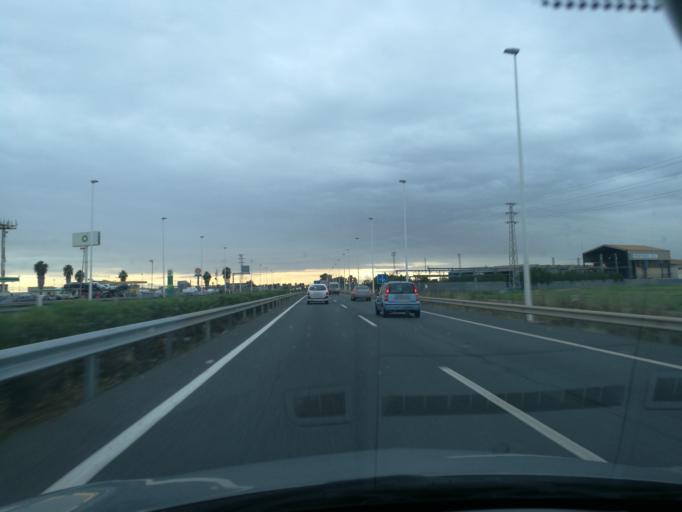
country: ES
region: Andalusia
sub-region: Provincia de Sevilla
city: Sevilla
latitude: 37.4294
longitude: -5.8937
